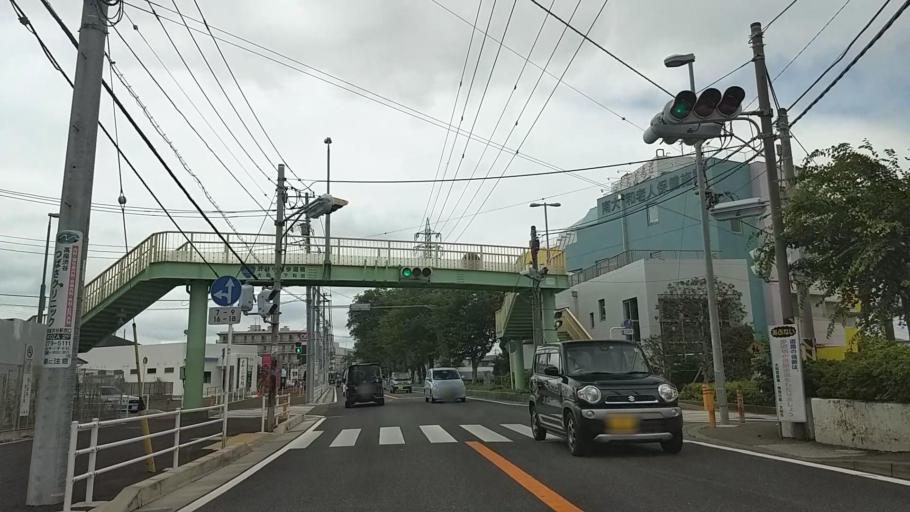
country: JP
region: Kanagawa
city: Minami-rinkan
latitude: 35.4313
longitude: 139.4680
